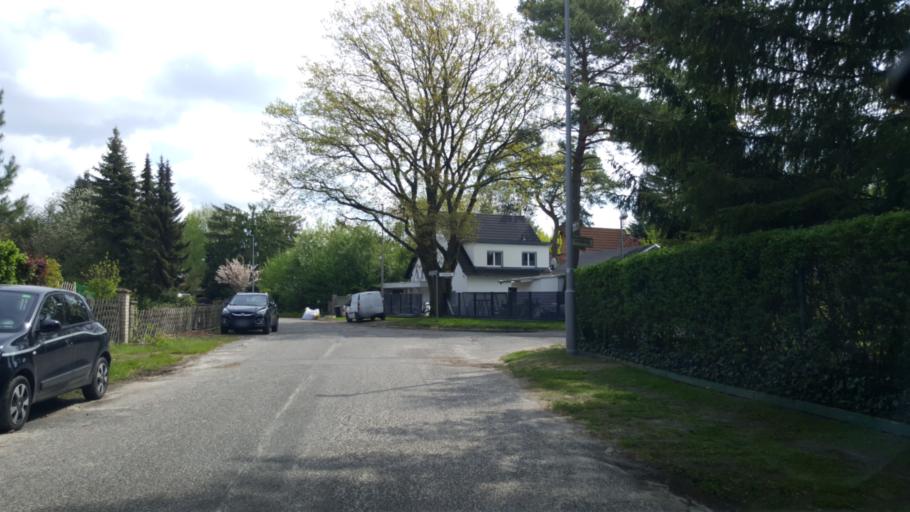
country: DE
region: Berlin
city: Bohnsdorf
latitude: 52.3926
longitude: 13.5808
